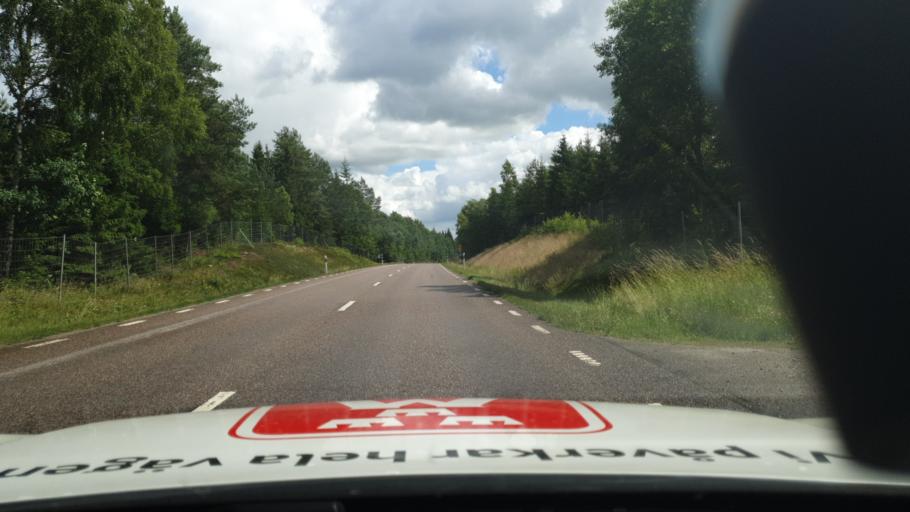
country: SE
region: Vaestra Goetaland
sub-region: Falkopings Kommun
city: Floby
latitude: 58.2047
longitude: 13.3029
